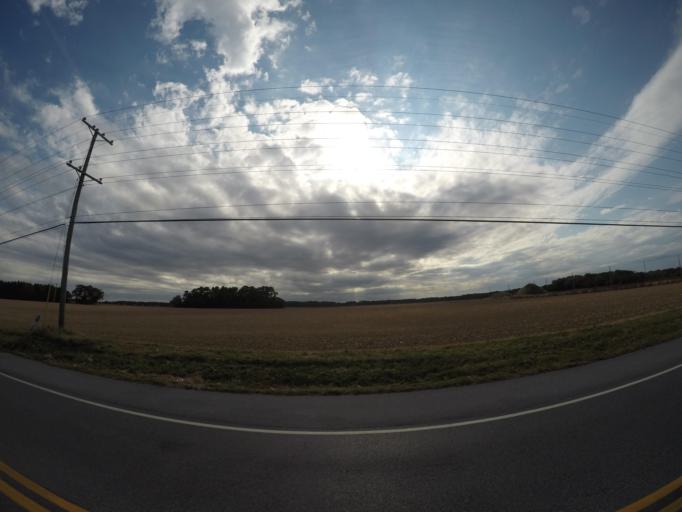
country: US
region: Delaware
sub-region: Sussex County
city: Lewes
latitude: 38.7304
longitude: -75.1499
